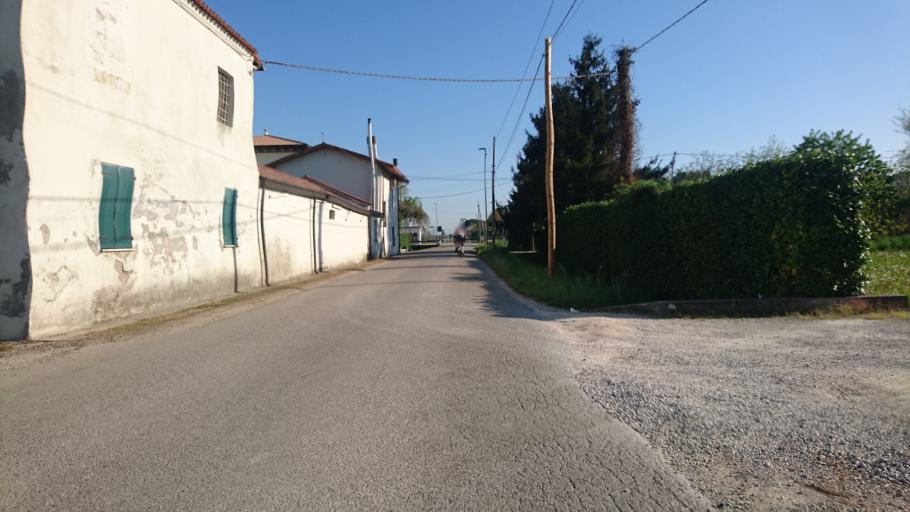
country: IT
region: Veneto
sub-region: Provincia di Venezia
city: Sant'Angelo
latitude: 45.5235
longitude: 11.9995
